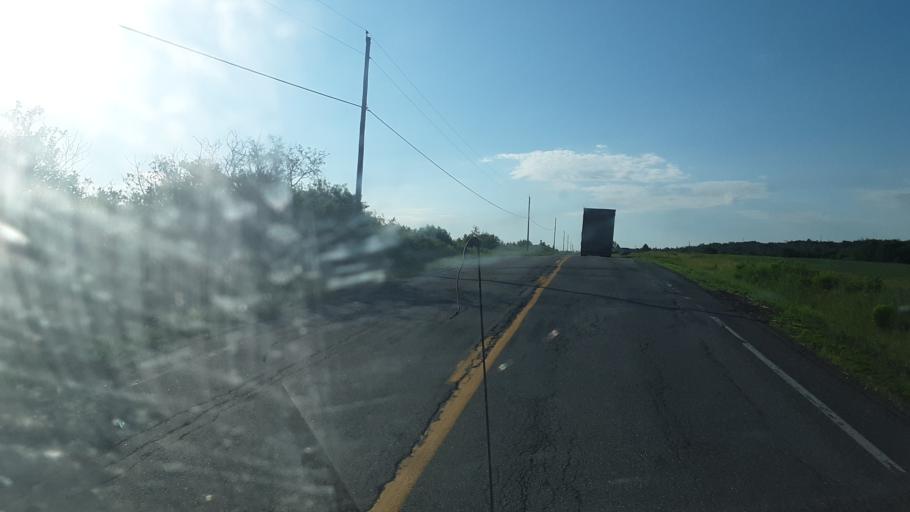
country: US
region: Maine
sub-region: Penobscot County
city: Patten
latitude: 46.1370
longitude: -68.1910
